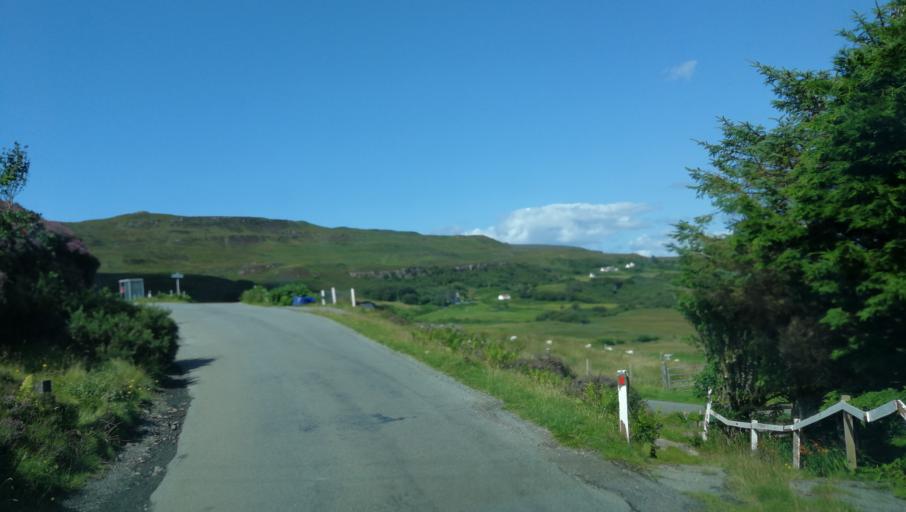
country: GB
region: Scotland
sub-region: Highland
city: Isle of Skye
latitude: 57.4527
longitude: -6.6598
